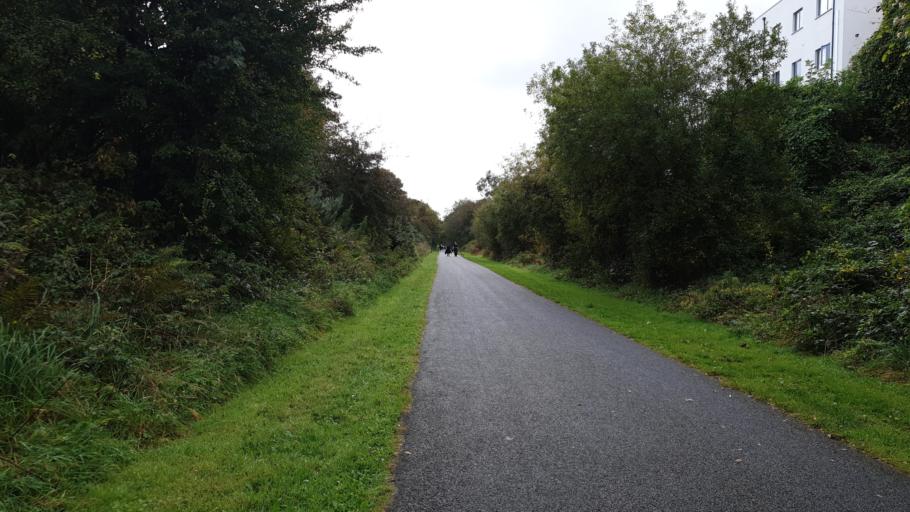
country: IE
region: Munster
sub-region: County Cork
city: Cork
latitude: 51.8930
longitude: -8.4147
